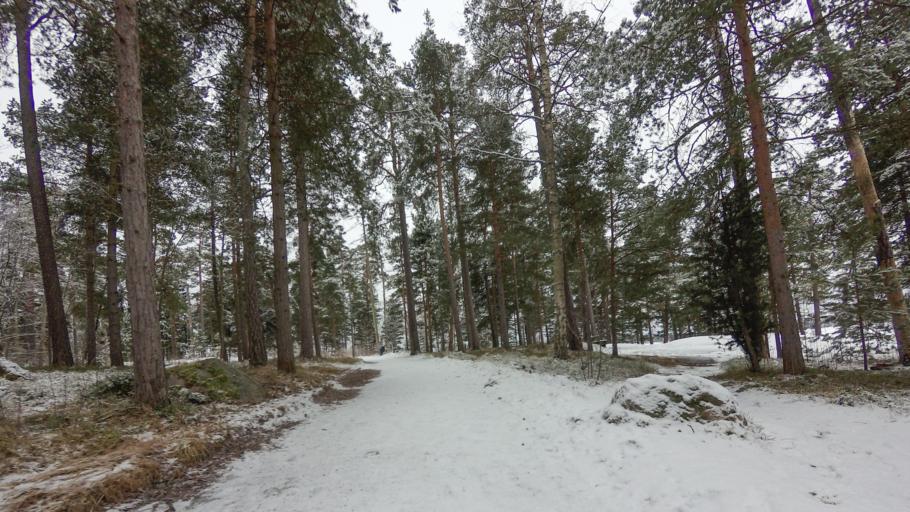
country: FI
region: Uusimaa
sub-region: Helsinki
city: Teekkarikylae
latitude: 60.1784
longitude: 24.8809
